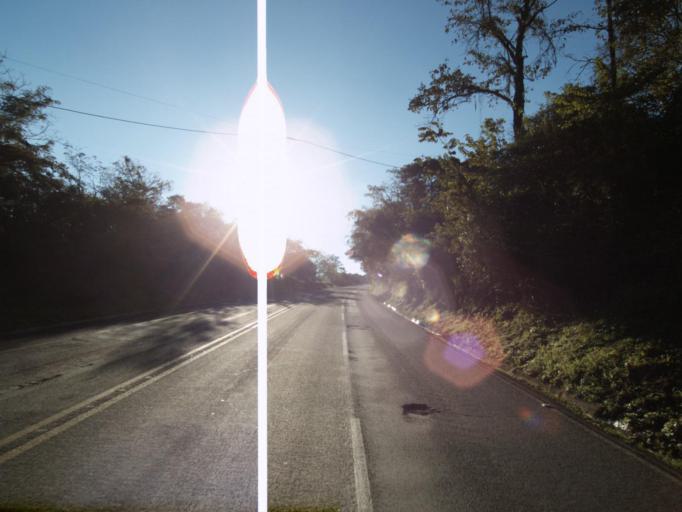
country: BR
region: Santa Catarina
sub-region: Chapeco
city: Chapeco
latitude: -26.9203
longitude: -52.8608
